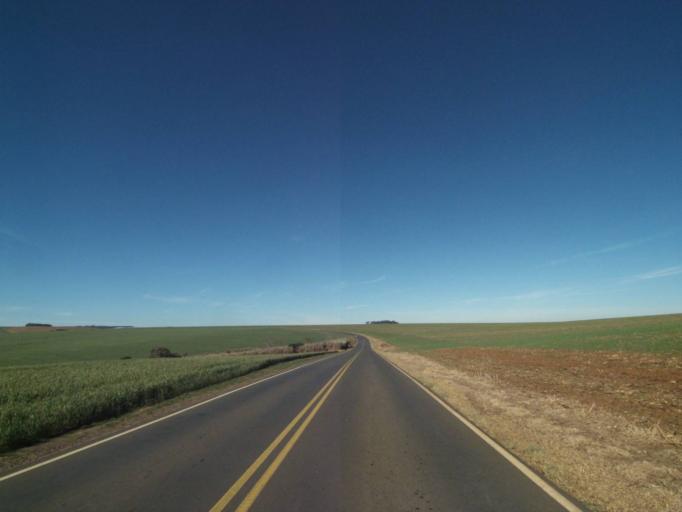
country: BR
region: Parana
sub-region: Tibagi
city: Tibagi
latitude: -24.5608
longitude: -50.2905
